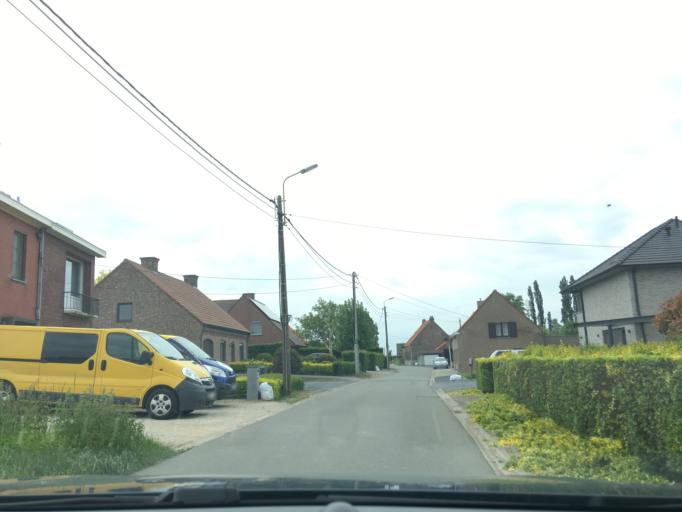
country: BE
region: Flanders
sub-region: Provincie West-Vlaanderen
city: Ledegem
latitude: 50.8883
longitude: 3.1059
